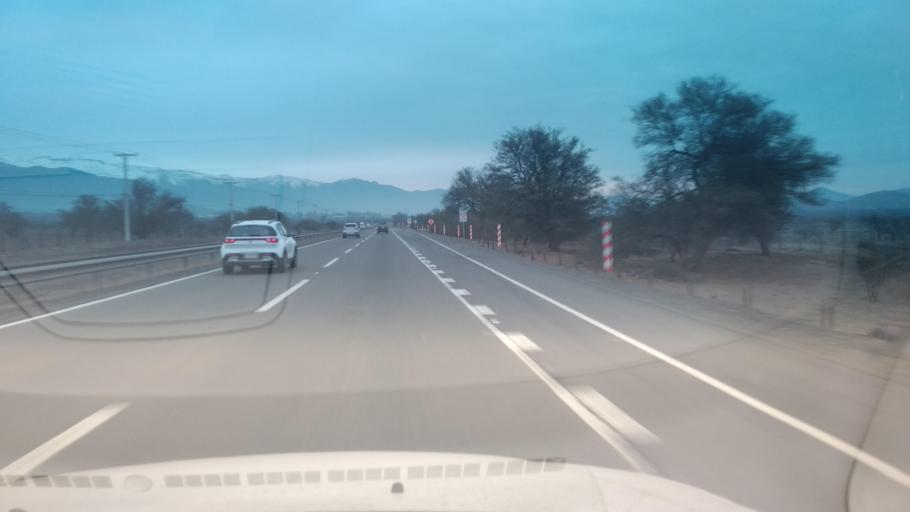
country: CL
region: Santiago Metropolitan
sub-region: Provincia de Chacabuco
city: Chicureo Abajo
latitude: -33.1217
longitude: -70.6780
